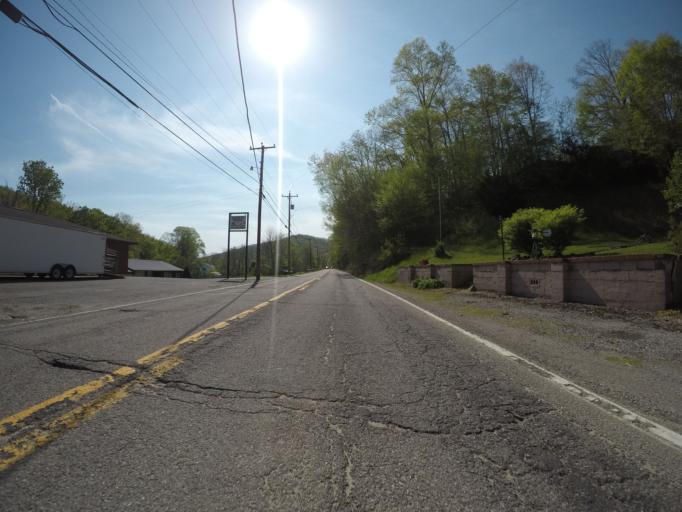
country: US
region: West Virginia
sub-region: Kanawha County
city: Clendenin
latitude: 38.4750
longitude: -81.3874
